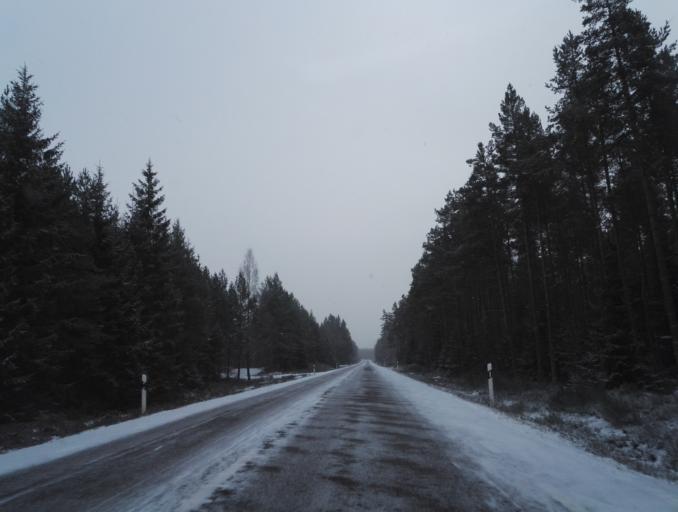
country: SE
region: Kronoberg
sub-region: Uppvidinge Kommun
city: Lenhovda
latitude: 56.8883
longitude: 15.3738
